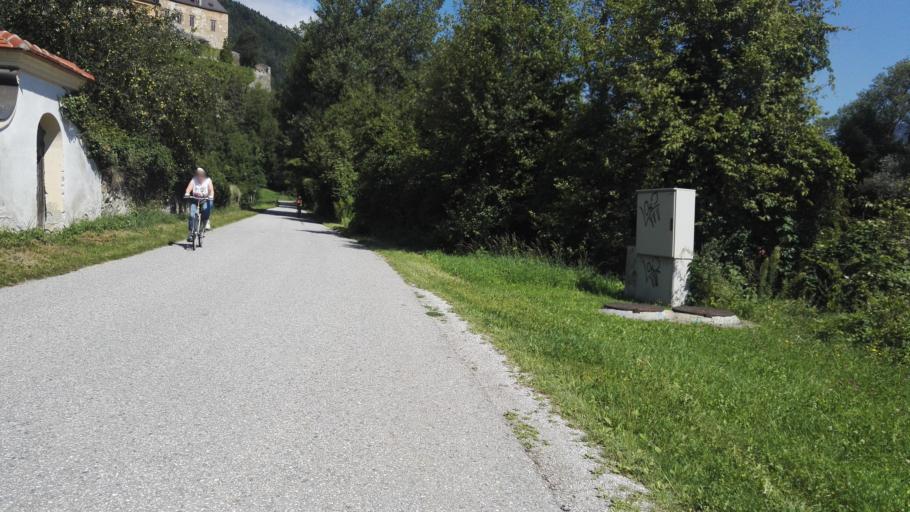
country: AT
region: Styria
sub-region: Politischer Bezirk Graz-Umgebung
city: Frohnleiten
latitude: 47.2443
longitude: 15.3111
